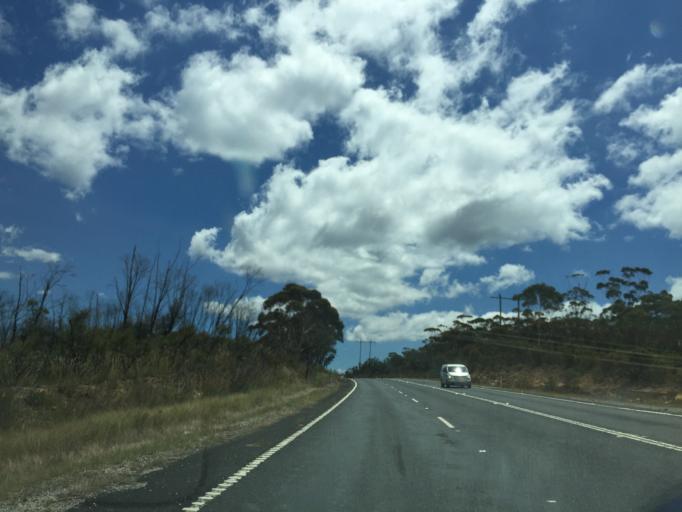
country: AU
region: New South Wales
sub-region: Blue Mountains Municipality
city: Blackheath
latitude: -33.5343
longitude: 150.3179
